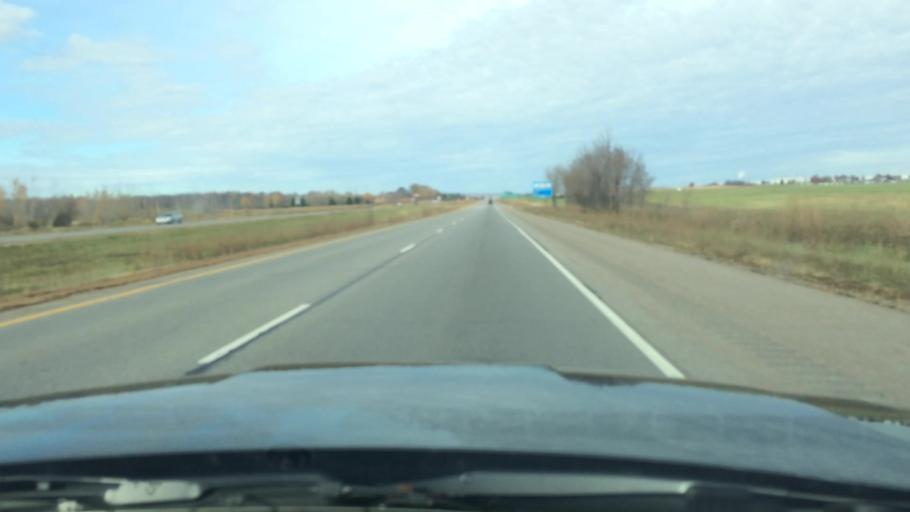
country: US
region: Wisconsin
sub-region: Marathon County
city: Mosinee
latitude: 44.7742
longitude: -89.6800
